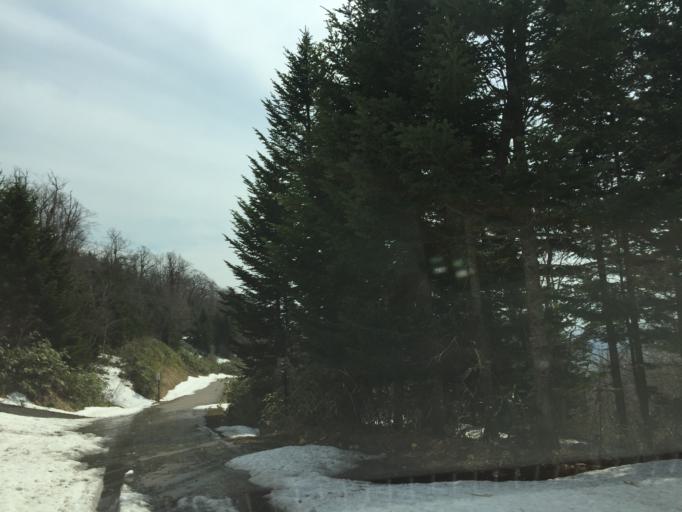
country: JP
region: Hokkaido
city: Akabira
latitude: 43.6077
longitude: 142.0684
